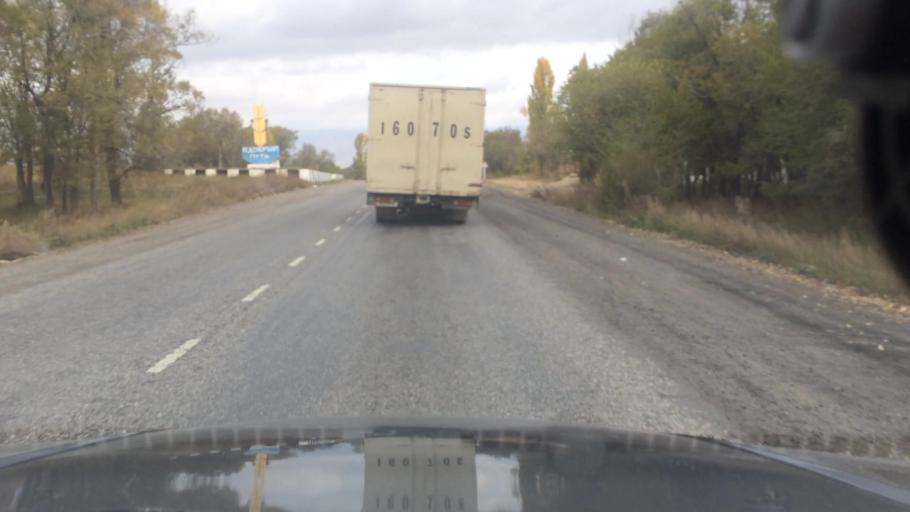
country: KG
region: Ysyk-Koel
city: Tyup
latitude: 42.6654
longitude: 78.3495
